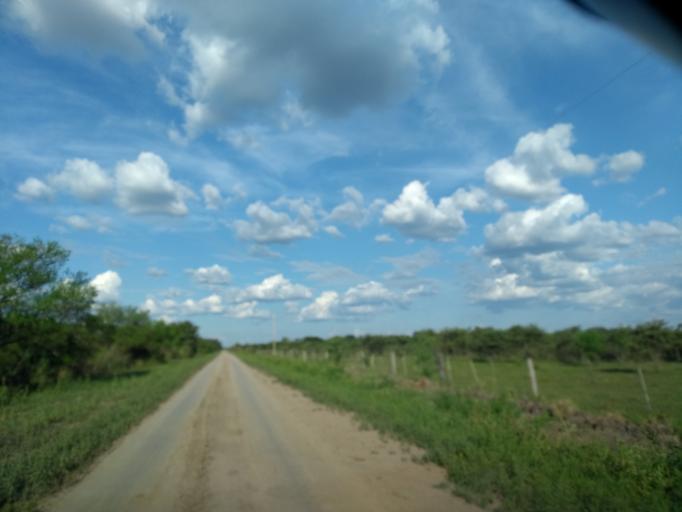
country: AR
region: Chaco
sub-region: Departamento de Quitilipi
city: Quitilipi
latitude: -26.7739
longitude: -60.1953
